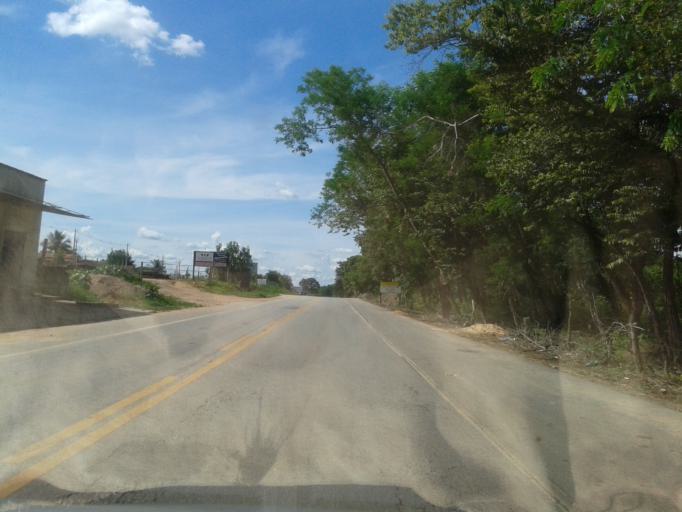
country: BR
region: Goias
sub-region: Itapuranga
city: Itapuranga
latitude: -15.4405
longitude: -50.3678
